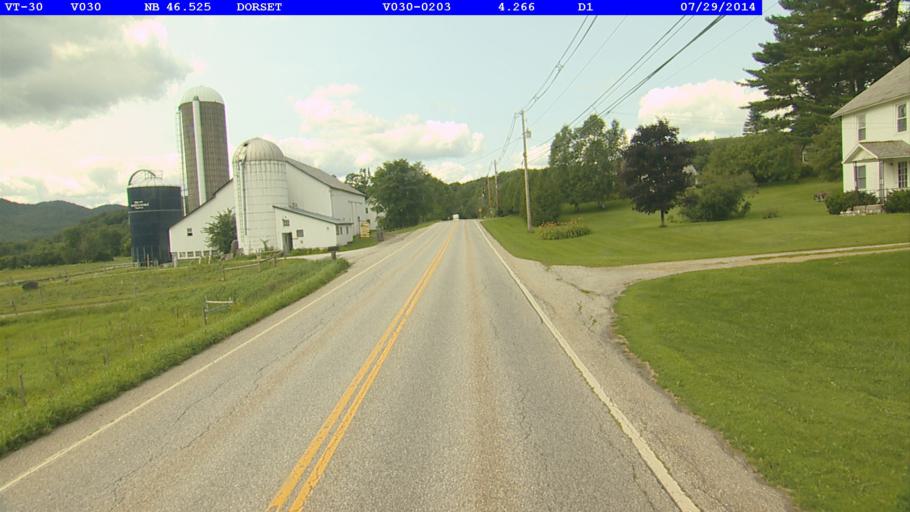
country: US
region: Vermont
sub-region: Bennington County
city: Manchester Center
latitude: 43.2662
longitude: -73.1069
